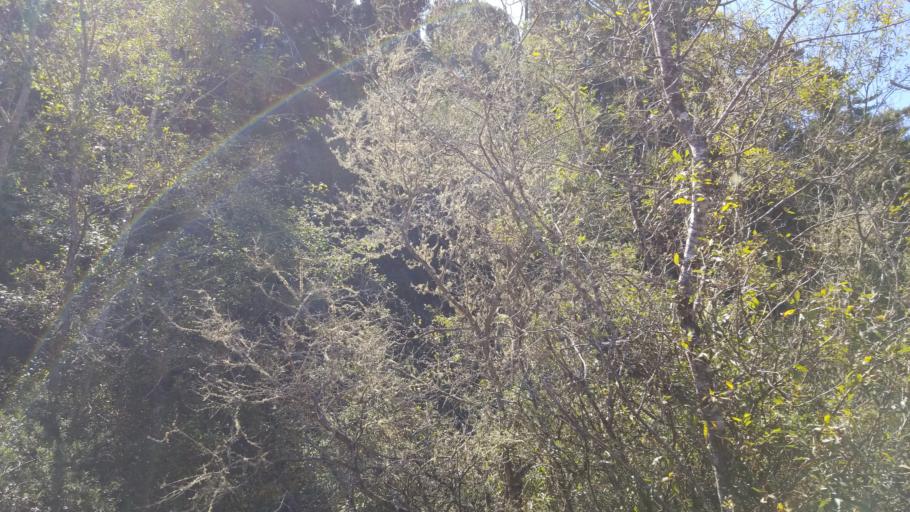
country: US
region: California
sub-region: Mendocino County
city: Fort Bragg
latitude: 39.4463
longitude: -123.7939
